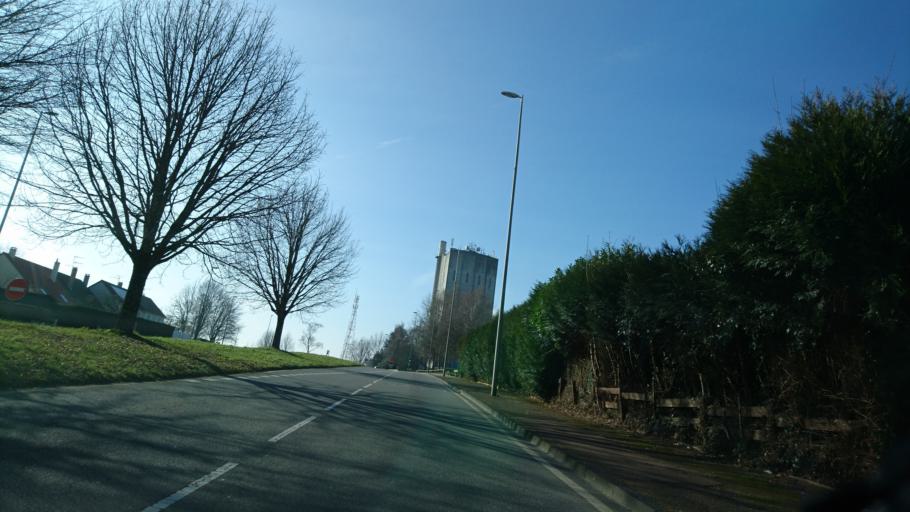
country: FR
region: Limousin
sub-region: Departement de la Haute-Vienne
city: Le Palais-sur-Vienne
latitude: 45.8741
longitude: 1.3003
